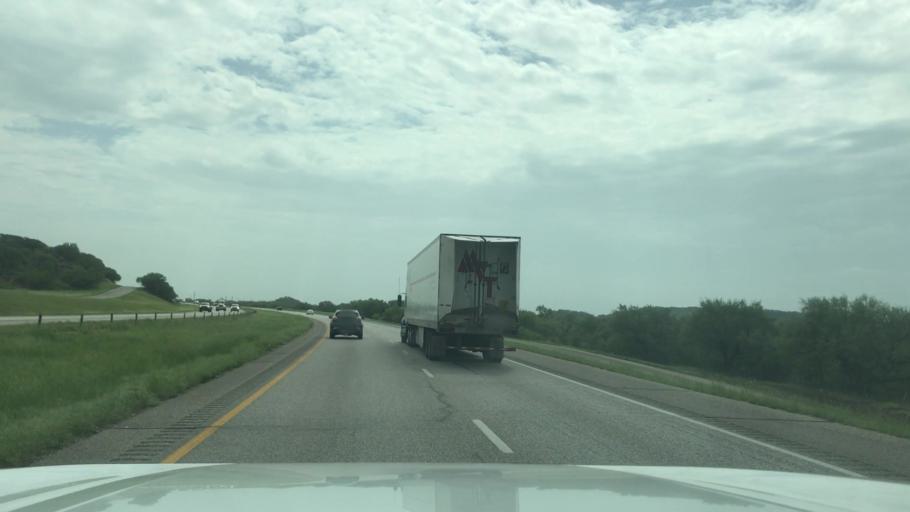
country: US
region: Texas
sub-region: Callahan County
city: Baird
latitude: 32.3703
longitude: -99.2157
